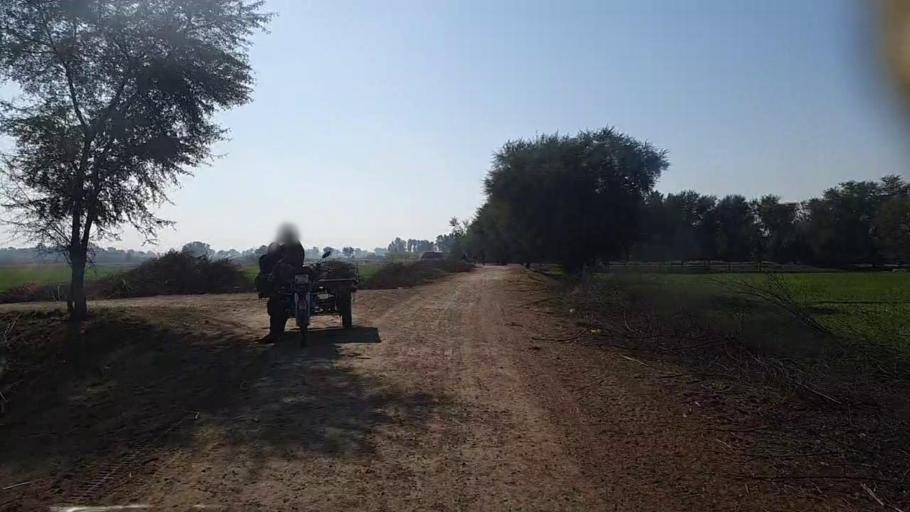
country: PK
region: Sindh
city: Khairpur
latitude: 28.0547
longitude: 69.7483
